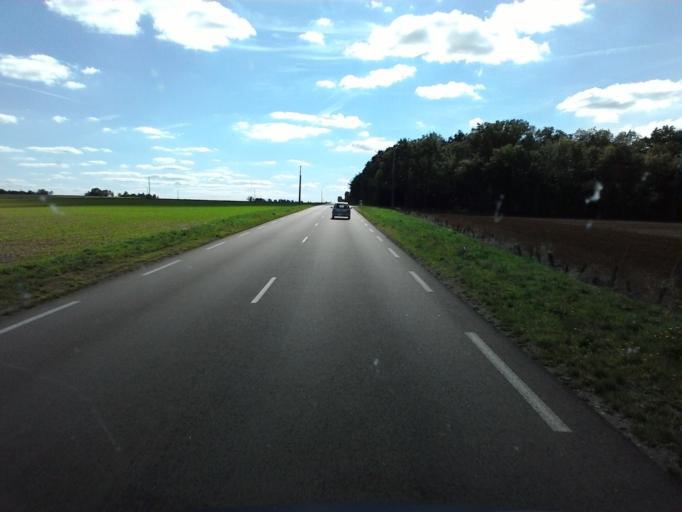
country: FR
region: Bourgogne
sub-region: Departement de la Cote-d'Or
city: Chatillon-sur-Seine
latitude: 47.8393
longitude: 4.5496
